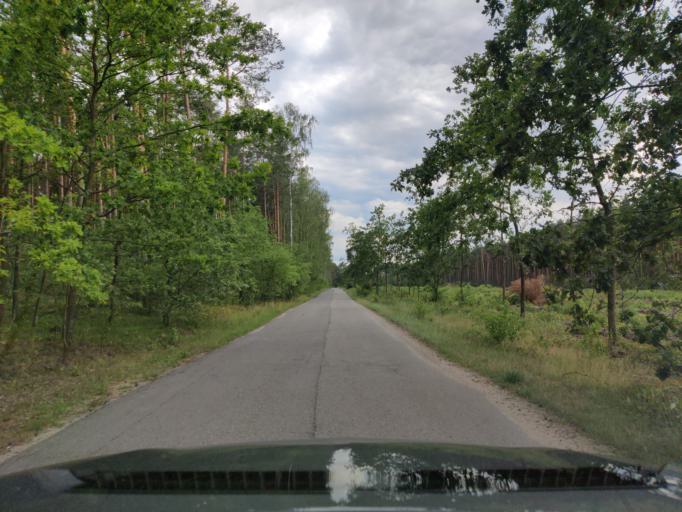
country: PL
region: Masovian Voivodeship
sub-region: Powiat pultuski
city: Pultusk
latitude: 52.7333
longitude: 21.1372
